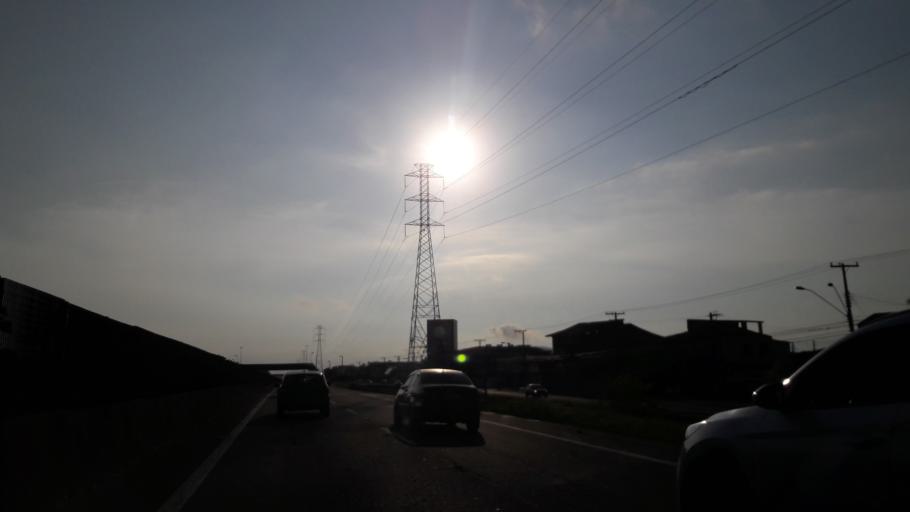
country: BR
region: Sao Paulo
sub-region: Mongagua
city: Mongagua
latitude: -24.1190
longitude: -46.6715
